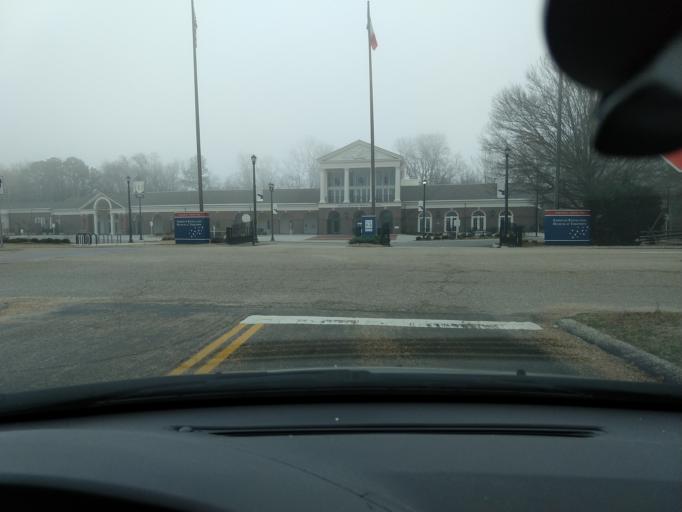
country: US
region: Virginia
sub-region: York County
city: Yorktown
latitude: 37.2399
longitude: -76.5185
